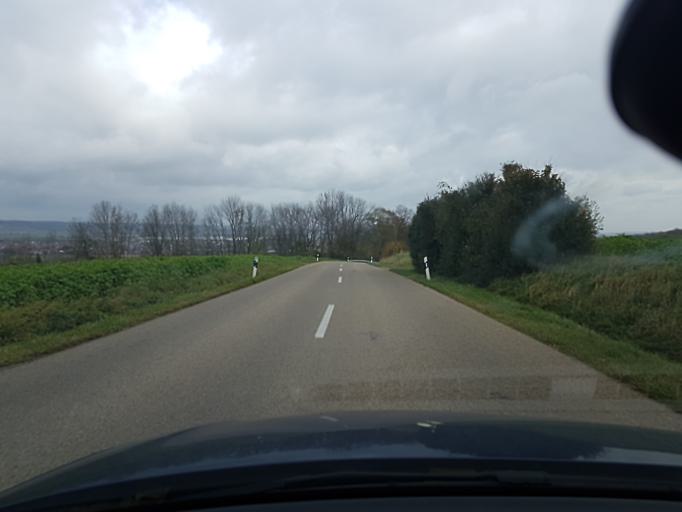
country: DE
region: Bavaria
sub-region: Lower Bavaria
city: Loiching
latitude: 48.6178
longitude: 12.4181
